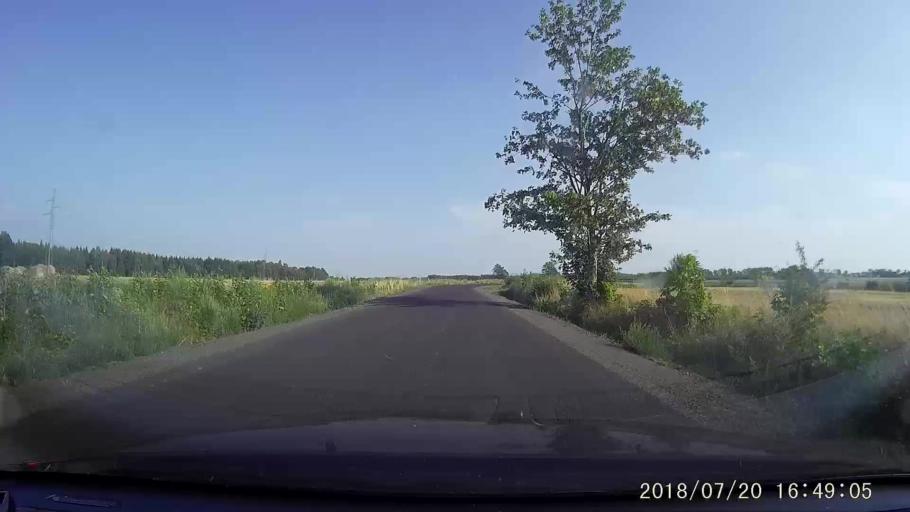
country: PL
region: Lower Silesian Voivodeship
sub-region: Powiat lubanski
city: Siekierczyn
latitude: 51.0508
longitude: 15.1941
